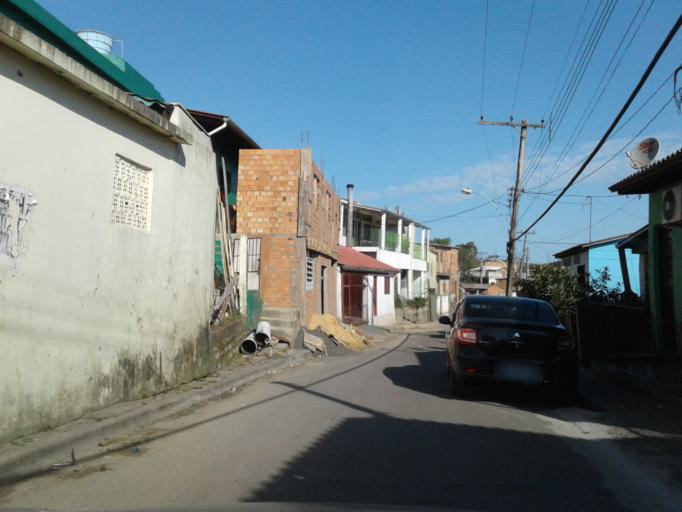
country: BR
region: Rio Grande do Sul
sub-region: Porto Alegre
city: Porto Alegre
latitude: -30.0461
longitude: -51.1509
